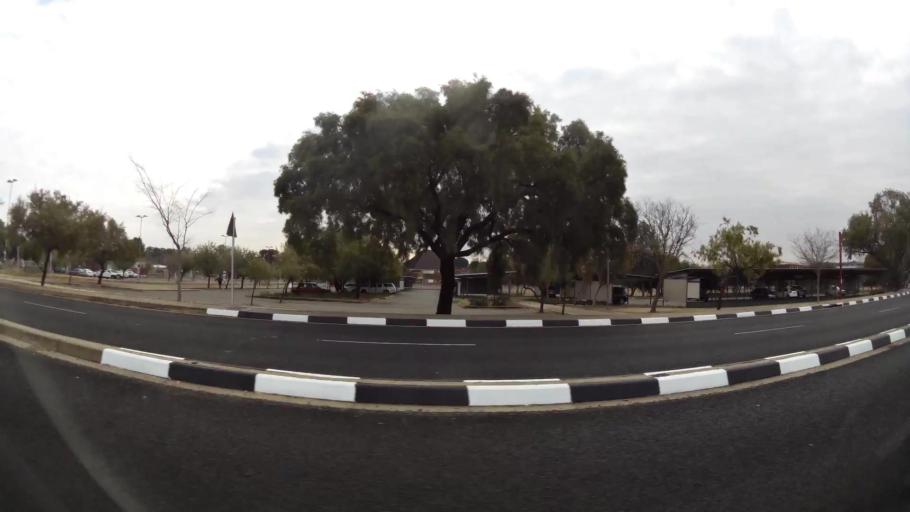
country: ZA
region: Orange Free State
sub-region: Mangaung Metropolitan Municipality
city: Bloemfontein
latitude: -29.1084
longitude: 26.1882
